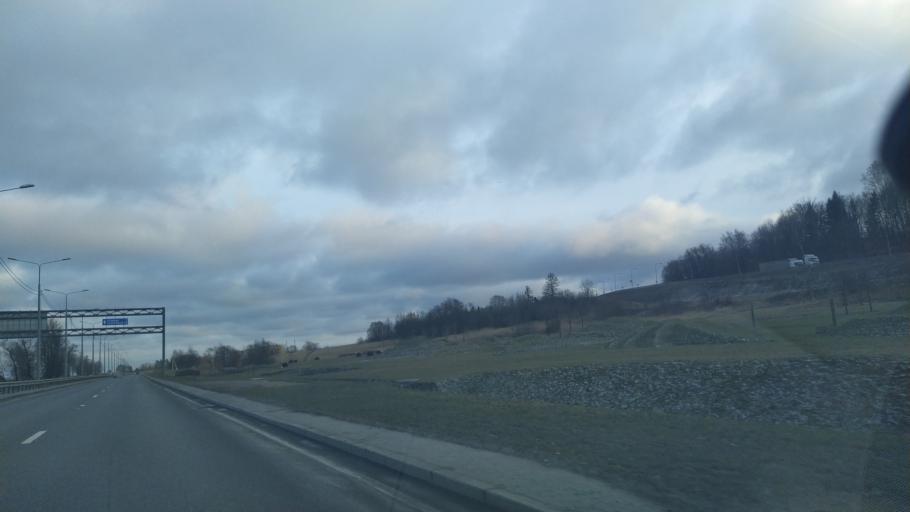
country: RU
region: St.-Petersburg
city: Aleksandrovskaya
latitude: 59.7757
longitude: 30.3300
